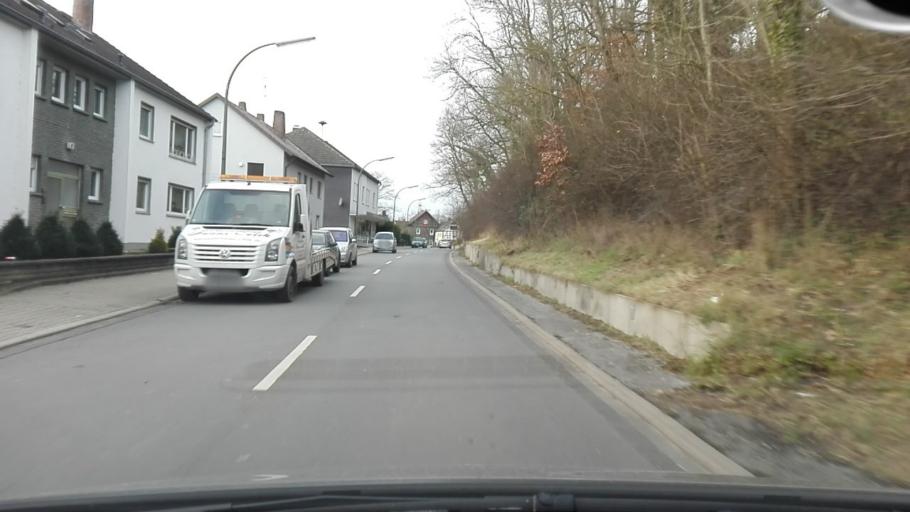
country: DE
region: North Rhine-Westphalia
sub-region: Regierungsbezirk Arnsberg
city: Unna
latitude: 51.4785
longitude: 7.6940
